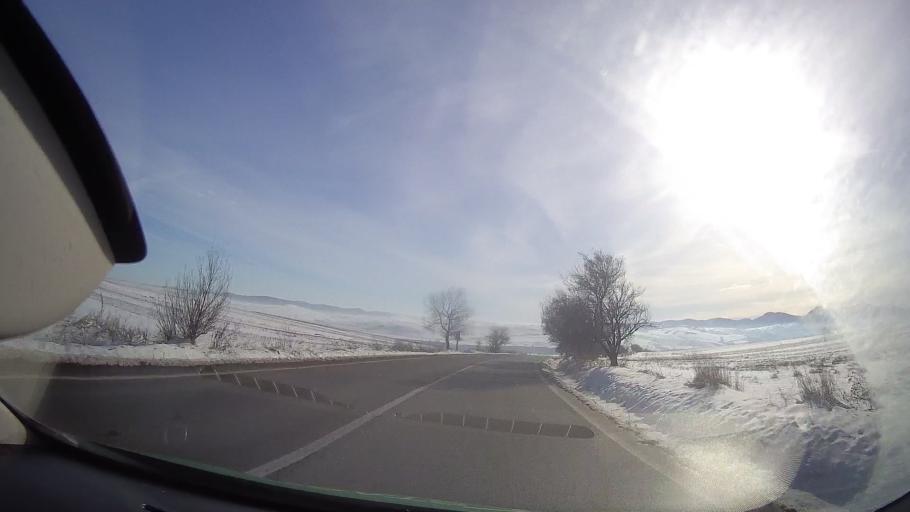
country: RO
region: Neamt
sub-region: Comuna Baltatesti
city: Valea Seaca
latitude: 47.1545
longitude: 26.3243
